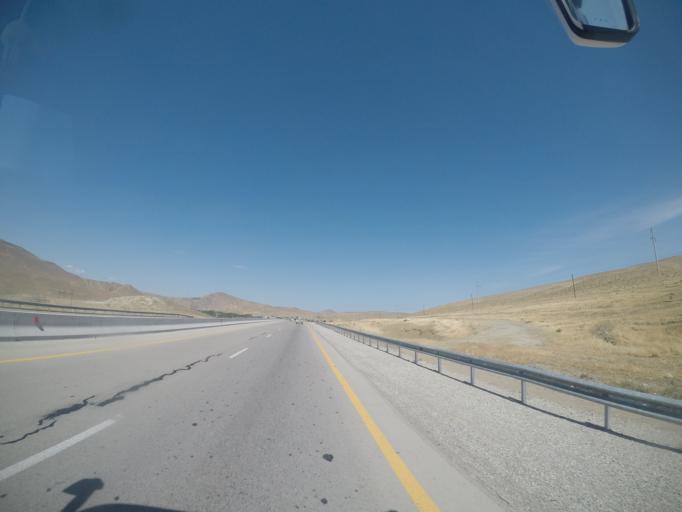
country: AZ
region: Sumqayit
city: Haci Zeynalabdin
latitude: 40.5010
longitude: 49.2821
